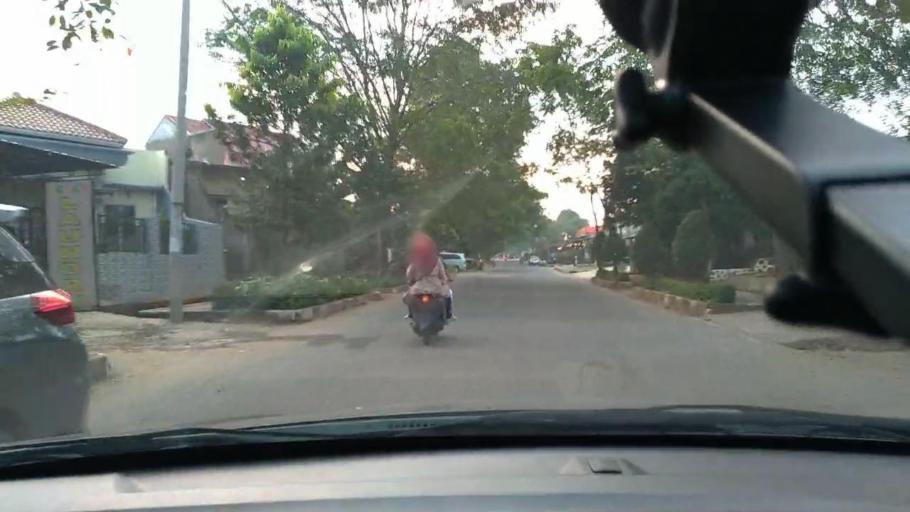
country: ID
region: West Java
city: Purwakarta
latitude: -6.5271
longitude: 107.4364
